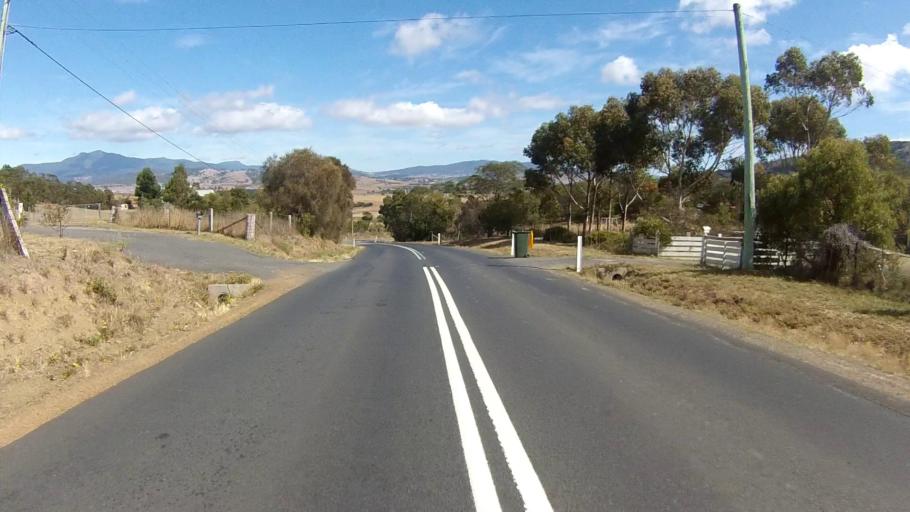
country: AU
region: Tasmania
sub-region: Glenorchy
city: Austins Ferry
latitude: -42.7276
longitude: 147.2872
